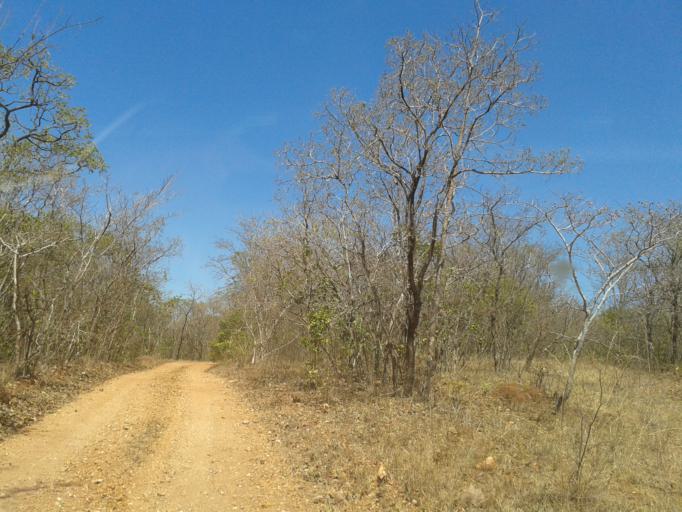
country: BR
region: Minas Gerais
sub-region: Ituiutaba
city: Ituiutaba
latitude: -19.1228
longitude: -49.2993
